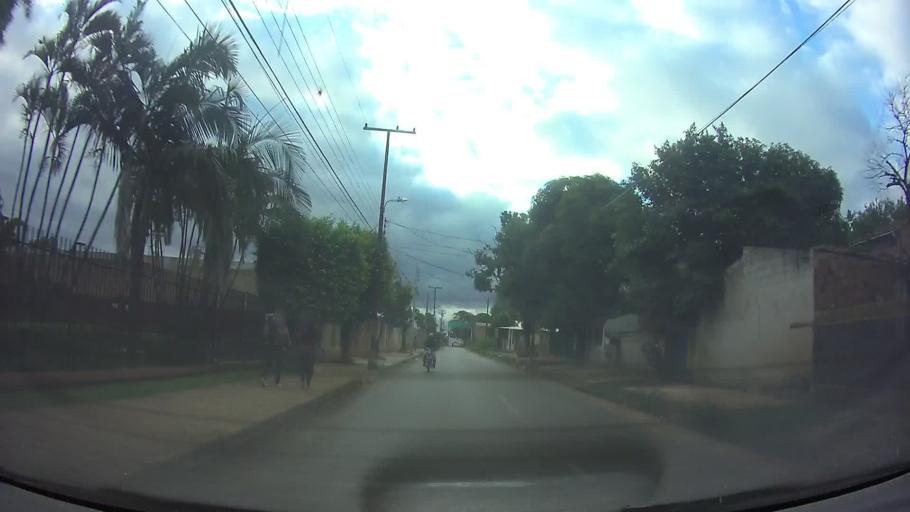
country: PY
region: Central
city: San Lorenzo
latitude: -25.3002
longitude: -57.5010
